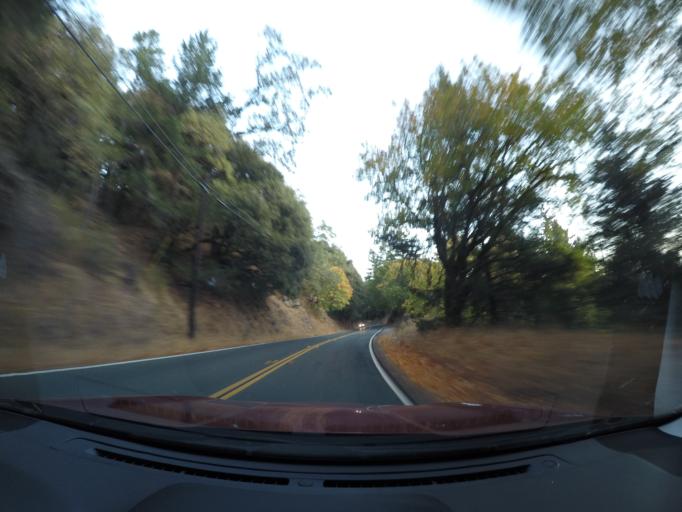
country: US
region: California
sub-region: Santa Clara County
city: Saratoga
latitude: 37.2184
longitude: -122.0732
